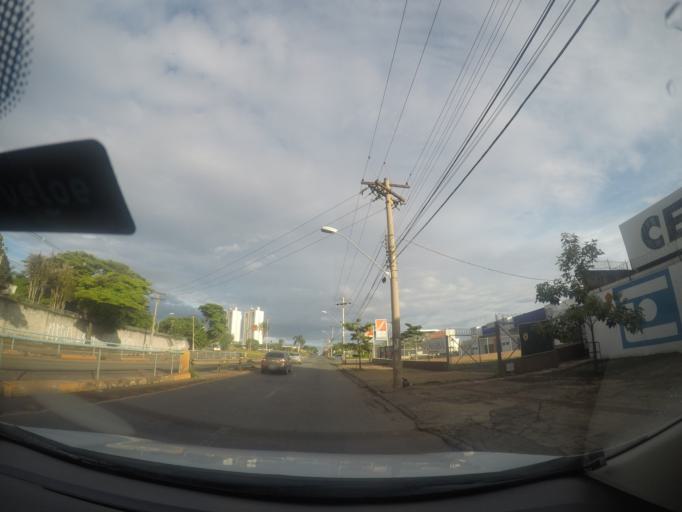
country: BR
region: Goias
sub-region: Goiania
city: Goiania
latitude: -16.6612
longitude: -49.3244
